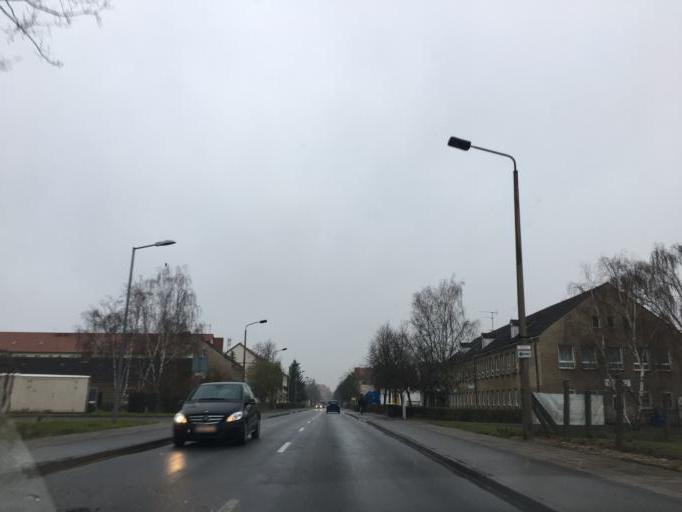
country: DE
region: Saxony-Anhalt
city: Haldensleben I
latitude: 52.2812
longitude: 11.4207
